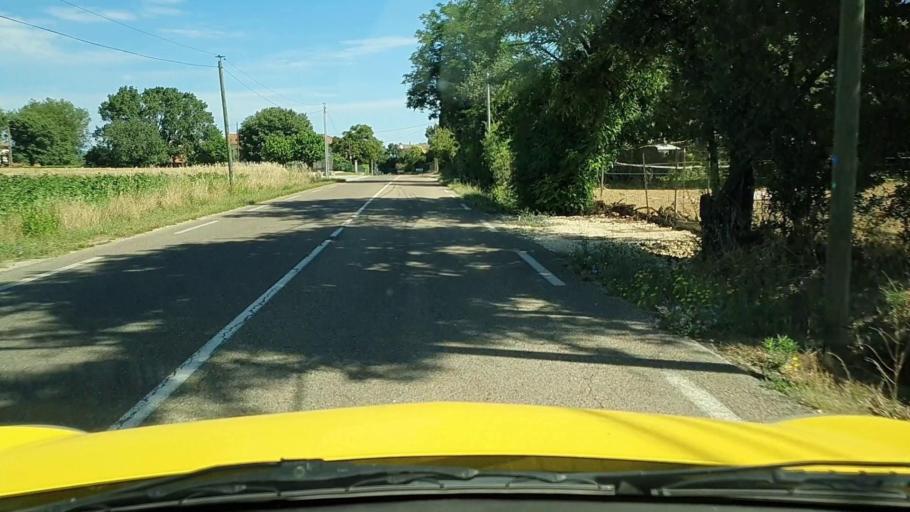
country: FR
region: Languedoc-Roussillon
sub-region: Departement du Gard
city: Saint-Hilaire-de-Brethmas
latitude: 44.0740
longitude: 4.1174
